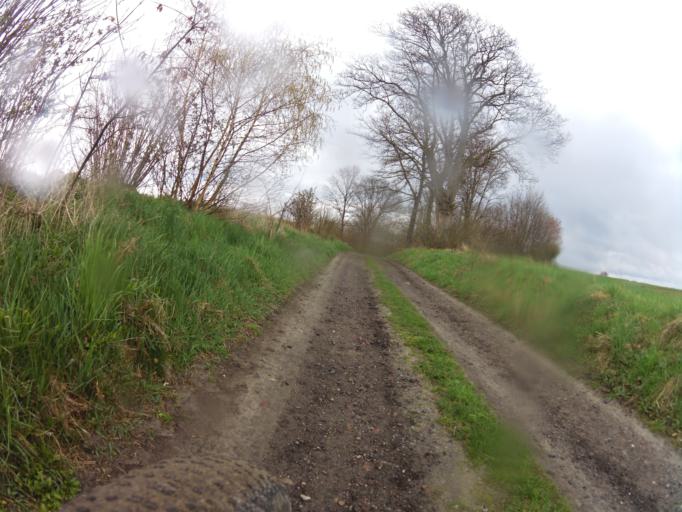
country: PL
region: West Pomeranian Voivodeship
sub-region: Powiat koszalinski
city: Polanow
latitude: 54.2152
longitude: 16.7605
